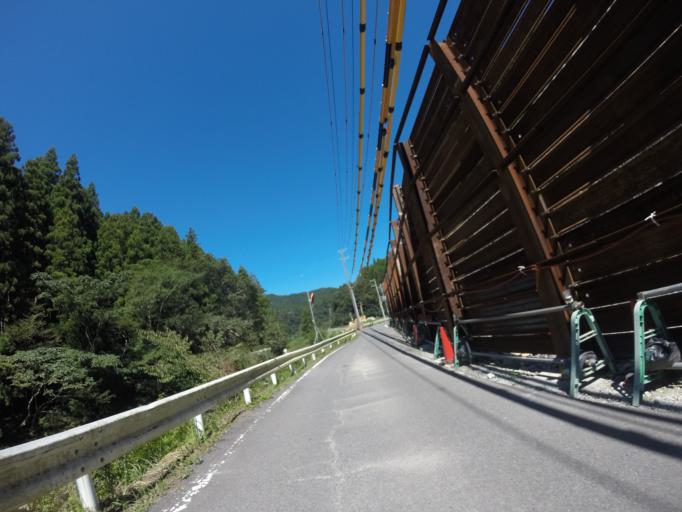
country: JP
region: Shizuoka
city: Kanaya
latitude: 34.9152
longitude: 138.1304
